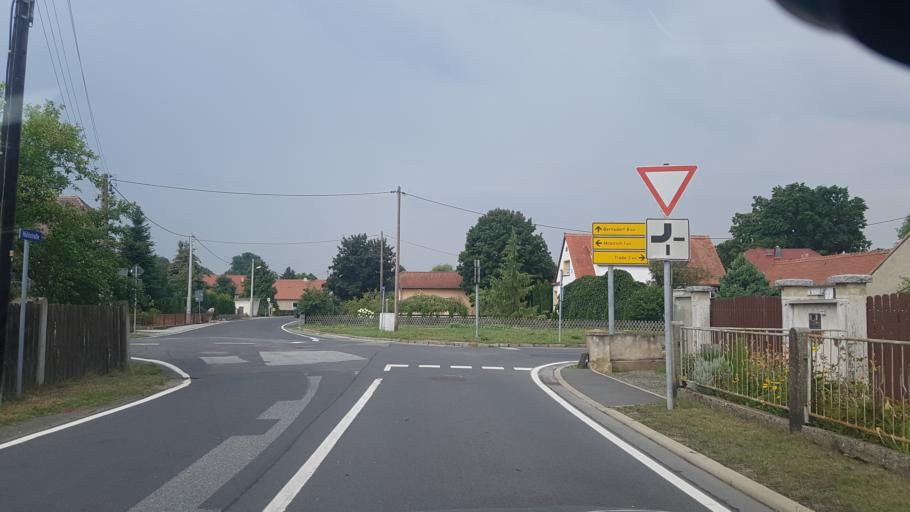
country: DE
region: Saxony
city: Ossling
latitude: 51.3327
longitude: 14.1730
